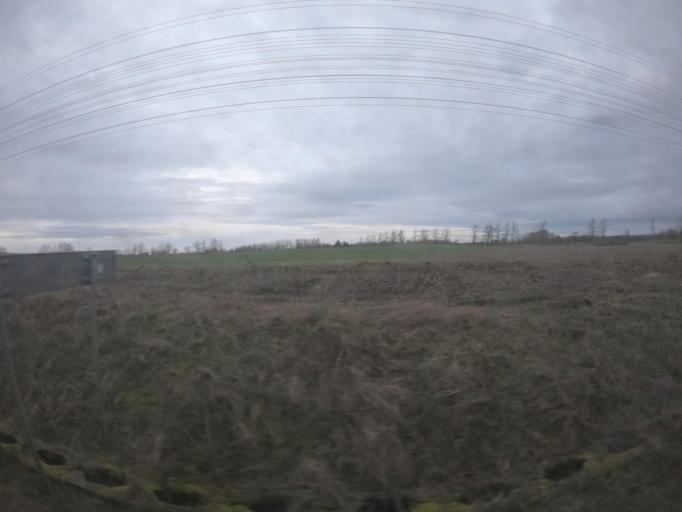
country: PL
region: West Pomeranian Voivodeship
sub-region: Powiat szczecinecki
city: Borne Sulinowo
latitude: 53.6311
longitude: 16.4839
